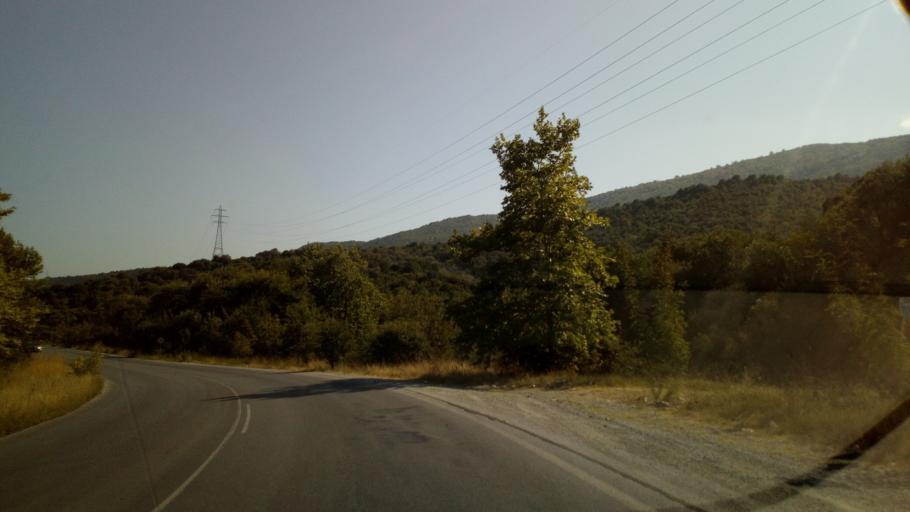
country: GR
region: Central Macedonia
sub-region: Nomos Thessalonikis
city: Stavros
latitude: 40.6482
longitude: 23.7445
